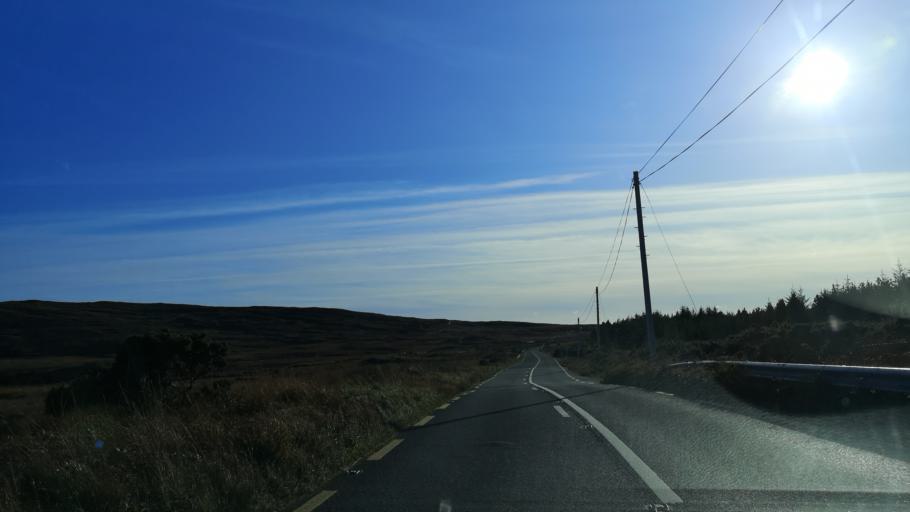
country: IE
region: Connaught
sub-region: County Galway
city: Clifden
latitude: 53.5360
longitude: -10.0374
